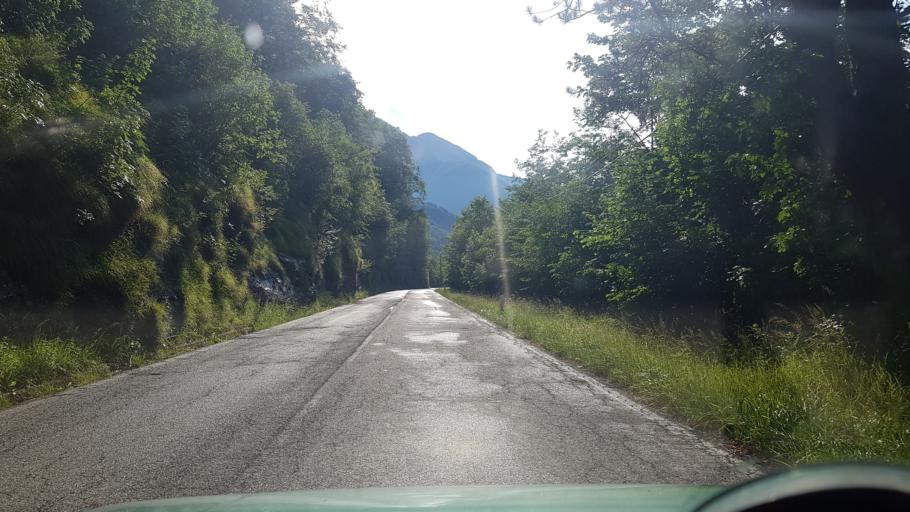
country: IT
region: Friuli Venezia Giulia
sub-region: Provincia di Udine
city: Lusevera
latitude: 46.3045
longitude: 13.3025
